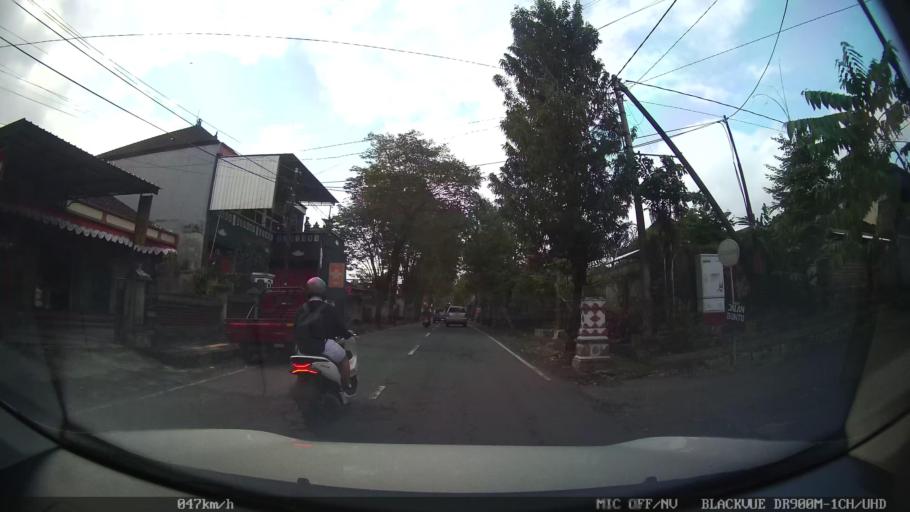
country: ID
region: Bali
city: Banjar Jambe Baleran
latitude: -8.5365
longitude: 115.1244
